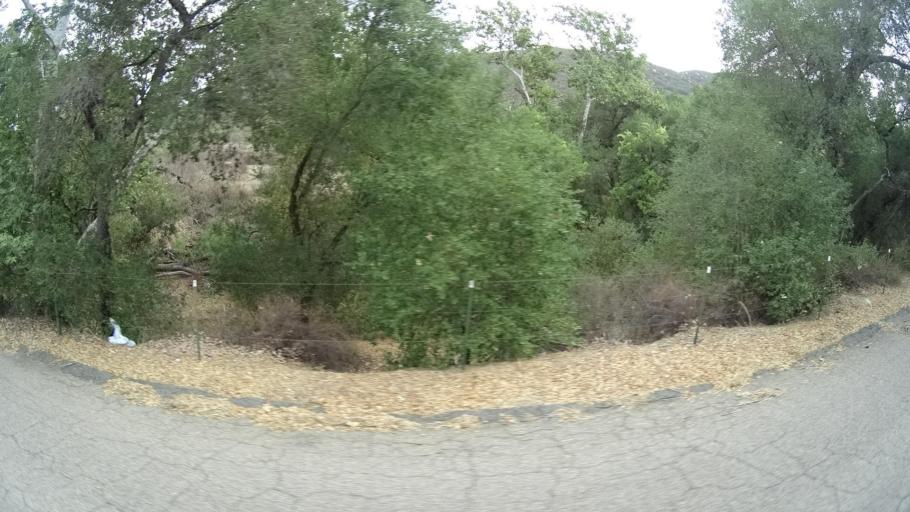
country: US
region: California
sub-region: San Diego County
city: Ramona
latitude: 33.1022
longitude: -116.8579
